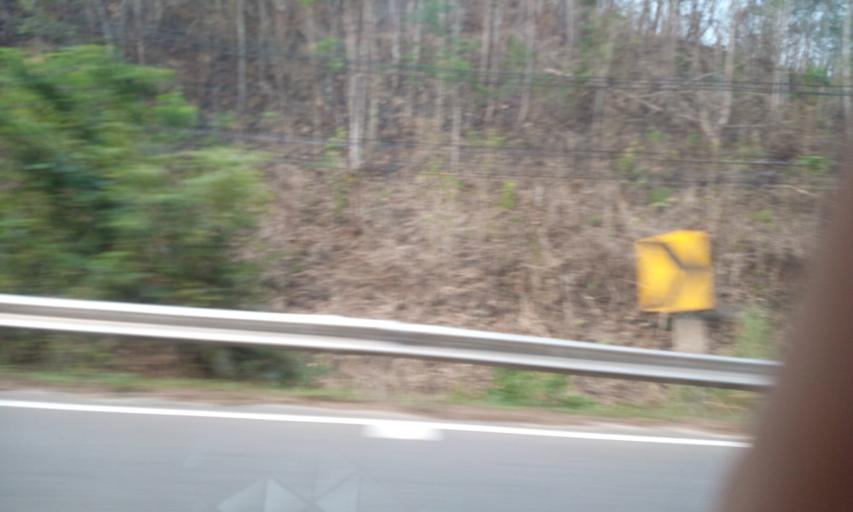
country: TH
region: Chiang Rai
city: Pa Daet
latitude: 19.6143
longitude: 100.0084
